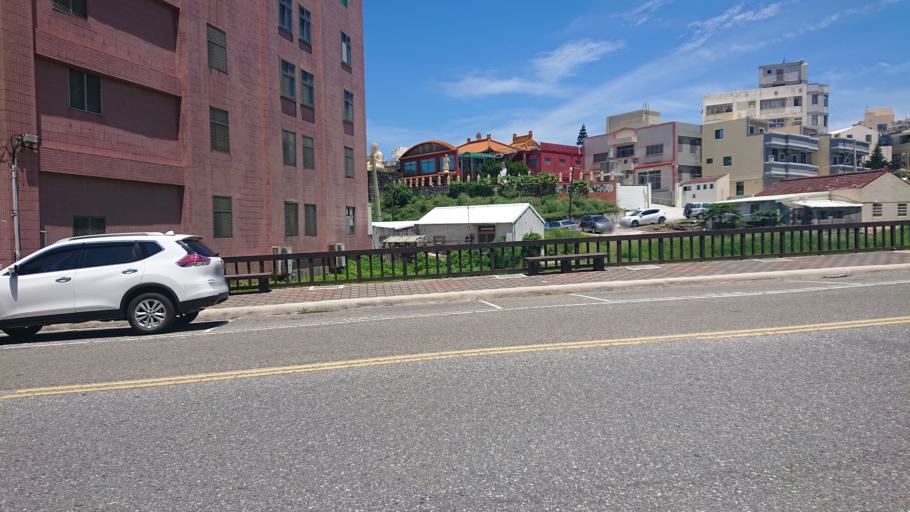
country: TW
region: Taiwan
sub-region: Penghu
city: Ma-kung
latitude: 23.5706
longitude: 119.5759
